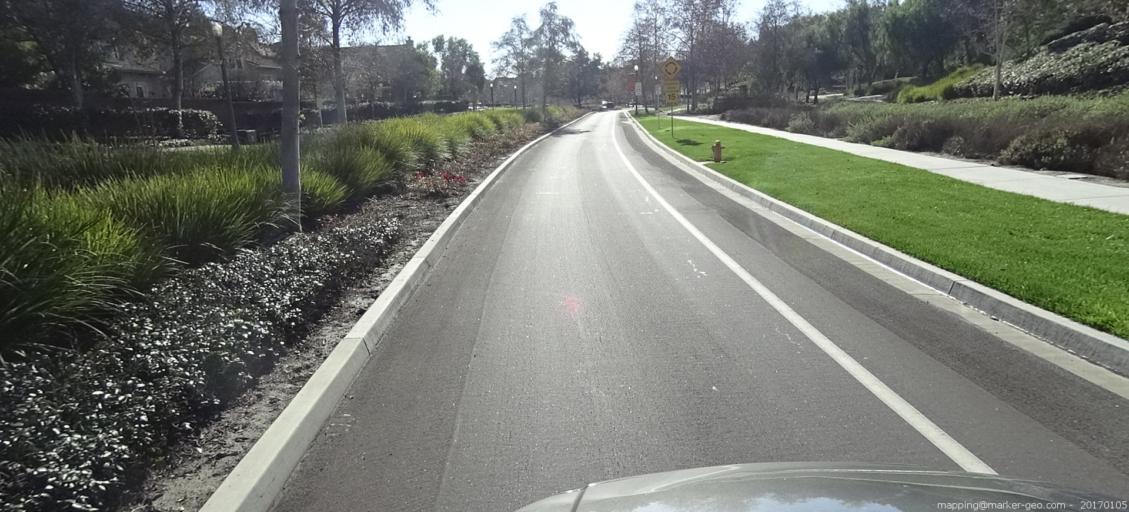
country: US
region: California
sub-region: Orange County
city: Ladera Ranch
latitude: 33.5564
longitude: -117.6362
